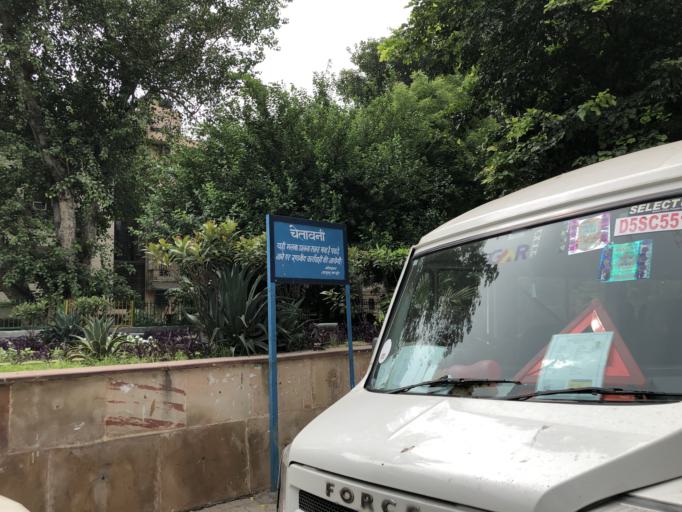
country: IN
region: NCT
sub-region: New Delhi
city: New Delhi
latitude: 28.5779
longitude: 77.2458
